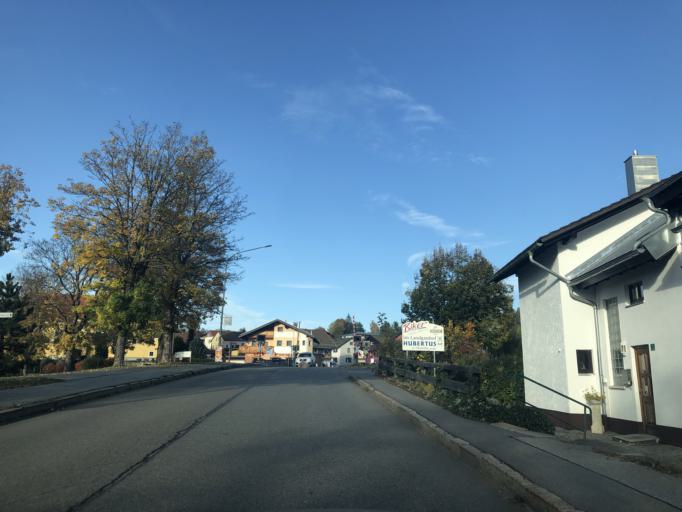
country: DE
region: Bavaria
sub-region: Lower Bavaria
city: Frauenau
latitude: 48.9879
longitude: 13.2993
